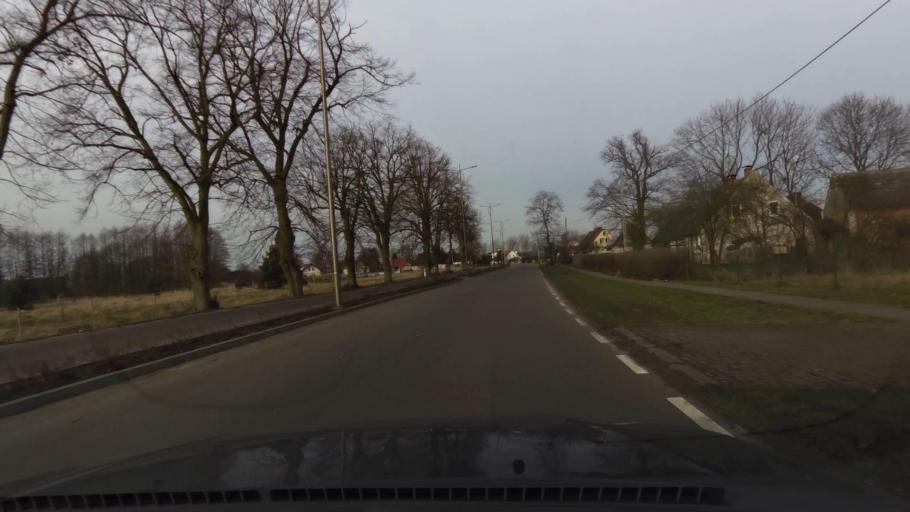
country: PL
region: West Pomeranian Voivodeship
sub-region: Powiat goleniowski
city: Stepnica
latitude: 53.6517
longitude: 14.6450
